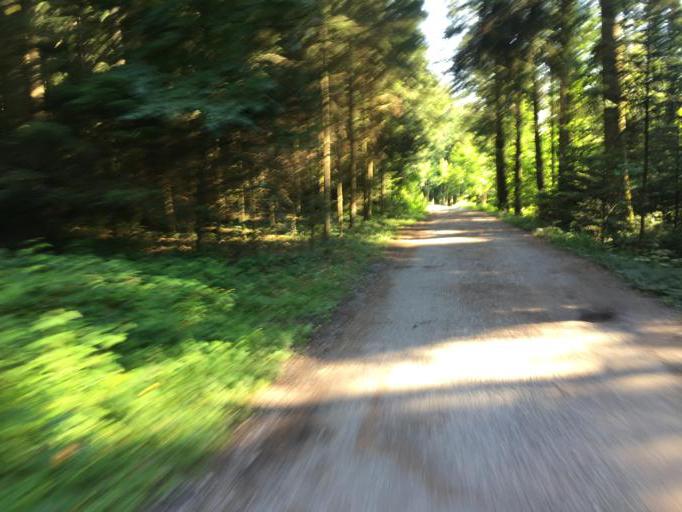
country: CH
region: Bern
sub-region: Bern-Mittelland District
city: Taegertschi
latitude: 46.8637
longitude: 7.5867
